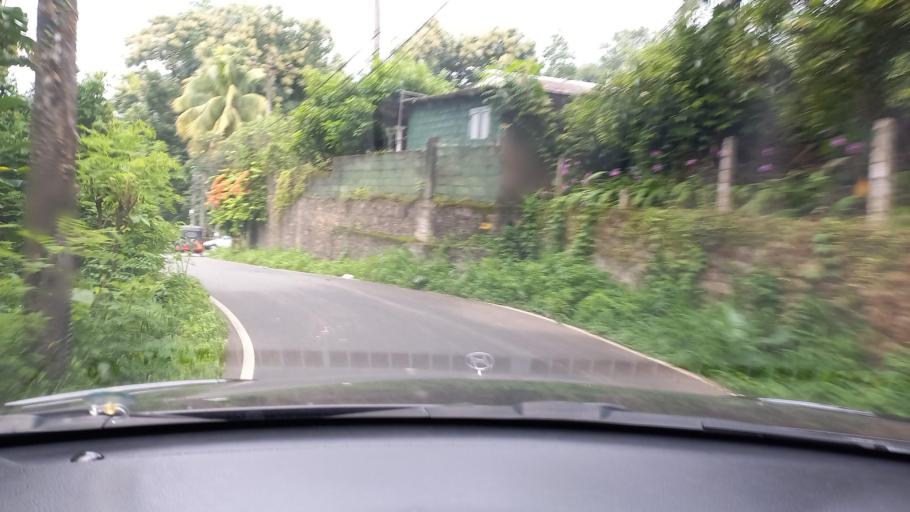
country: LK
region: Central
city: Kadugannawa
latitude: 7.2578
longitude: 80.3504
